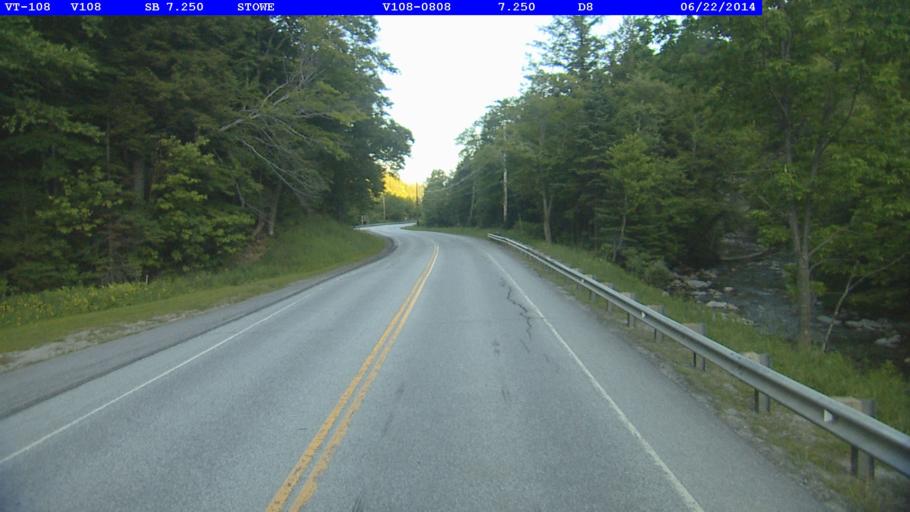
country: US
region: Vermont
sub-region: Lamoille County
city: Johnson
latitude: 44.5266
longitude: -72.7790
